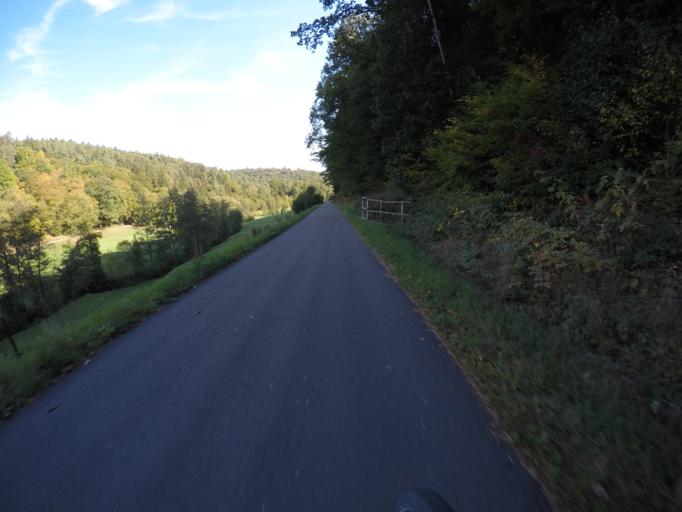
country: DE
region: Baden-Wuerttemberg
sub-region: Regierungsbezirk Stuttgart
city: Waldenbuch
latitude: 48.6457
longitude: 9.1628
